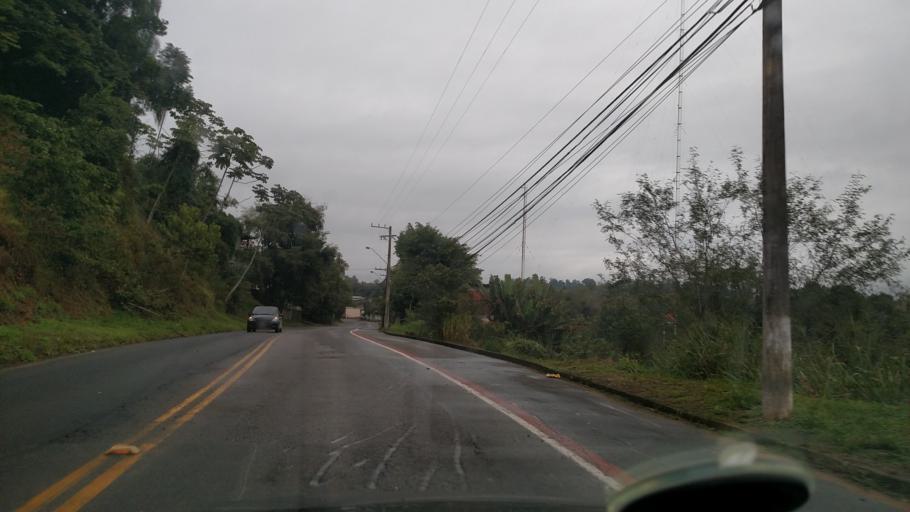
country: BR
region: Santa Catarina
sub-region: Blumenau
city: Blumenau
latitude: -26.8668
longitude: -49.0837
